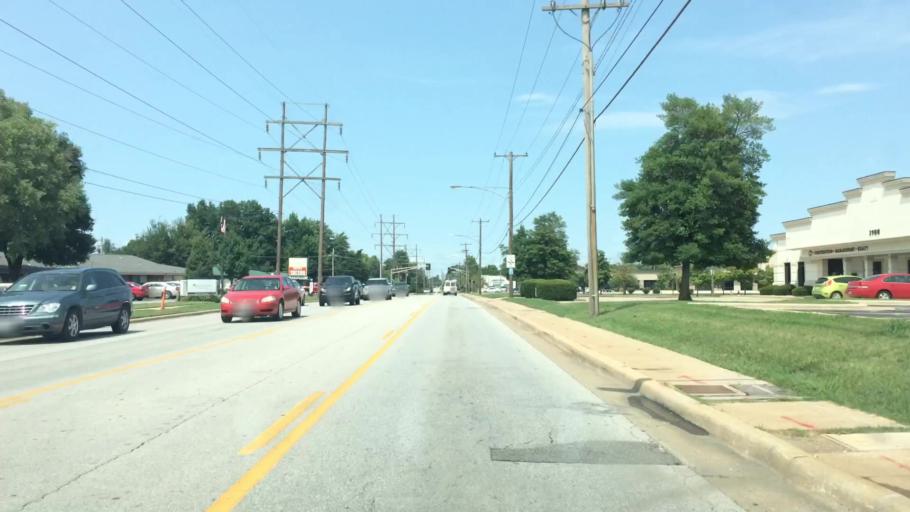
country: US
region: Missouri
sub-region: Greene County
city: Springfield
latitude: 37.1609
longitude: -93.2717
